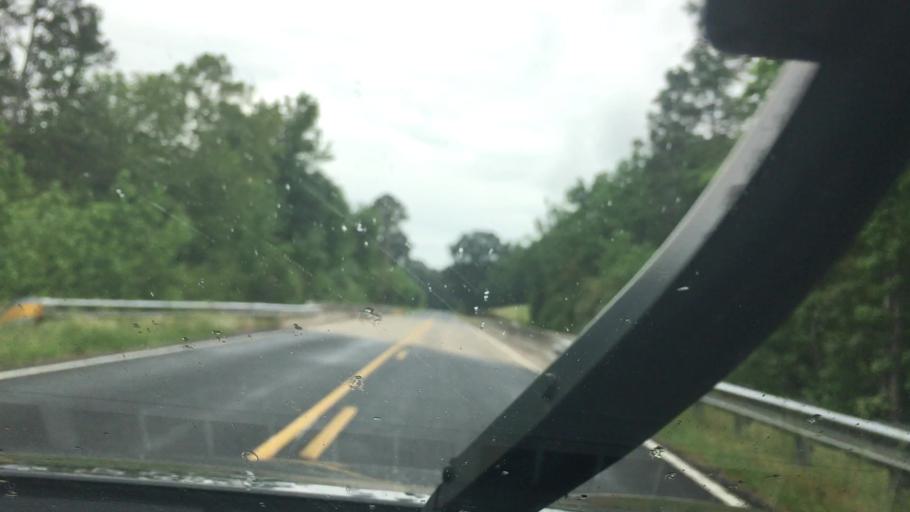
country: US
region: North Carolina
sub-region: Stanly County
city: Badin
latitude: 35.3646
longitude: -80.1160
